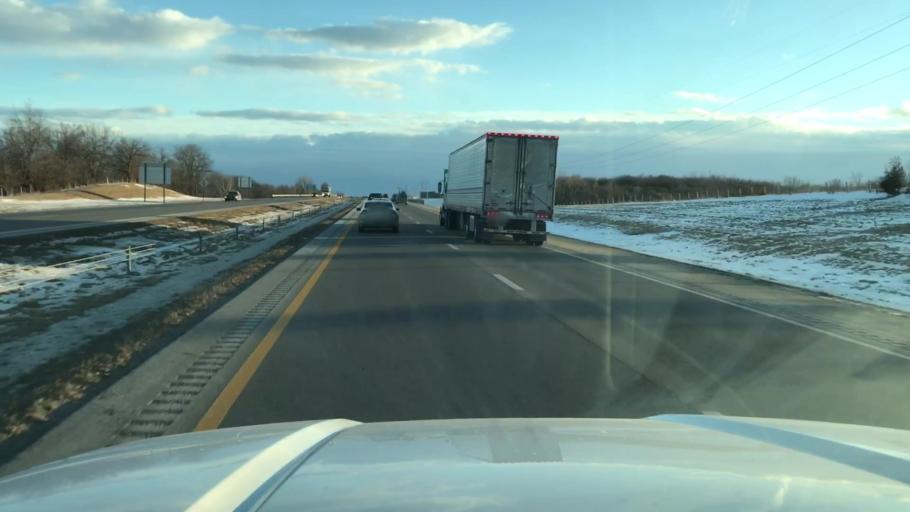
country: US
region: Missouri
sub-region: Buchanan County
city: Saint Joseph
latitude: 39.7681
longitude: -94.7925
